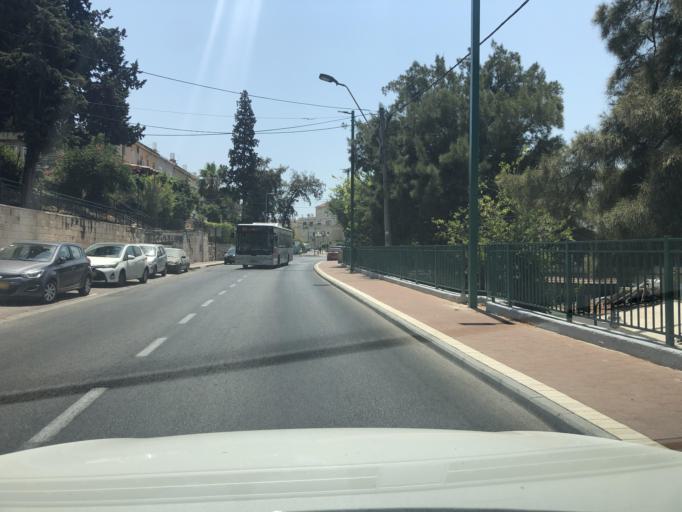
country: IL
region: Haifa
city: Daliyat el Karmil
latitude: 32.6561
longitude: 35.1065
